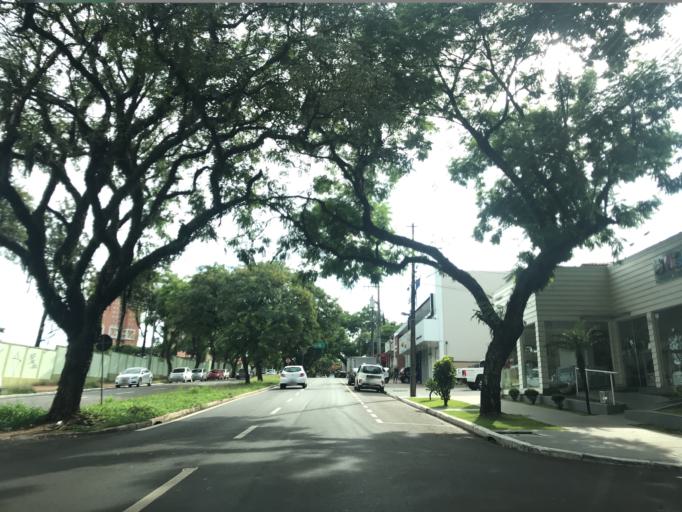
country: BR
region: Parana
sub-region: Maringa
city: Maringa
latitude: -23.4350
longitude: -51.9313
